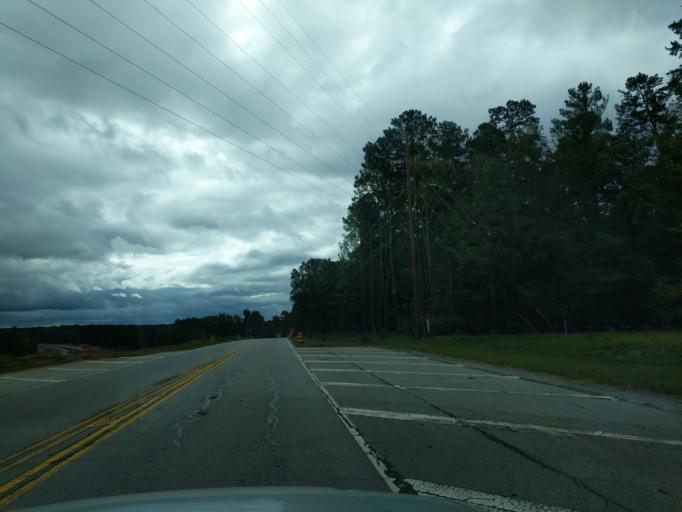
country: US
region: Georgia
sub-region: Wilkes County
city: Washington
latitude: 33.6965
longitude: -82.6846
